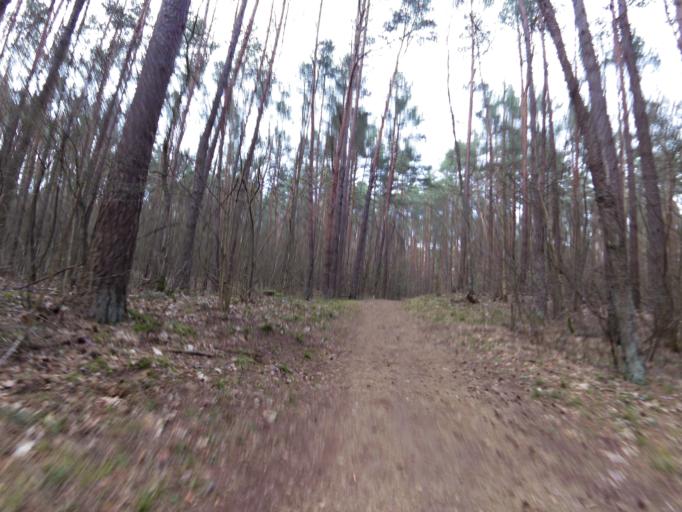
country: LT
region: Vilnius County
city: Pilaite
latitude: 54.6939
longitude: 25.1937
